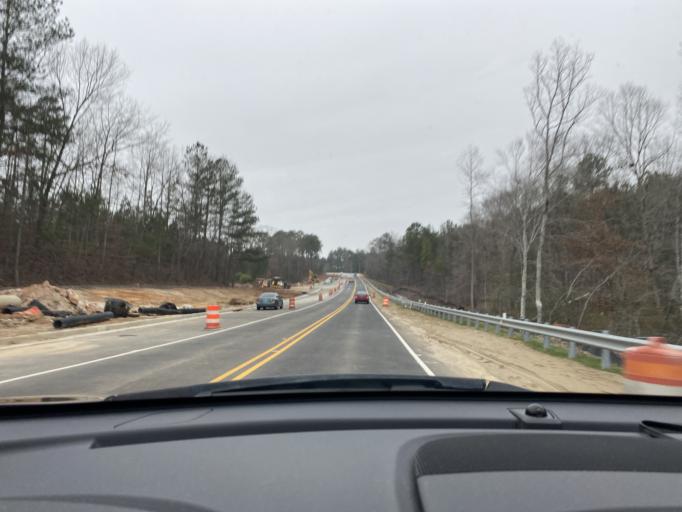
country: US
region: Georgia
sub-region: Gwinnett County
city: Grayson
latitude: 33.9175
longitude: -83.8893
